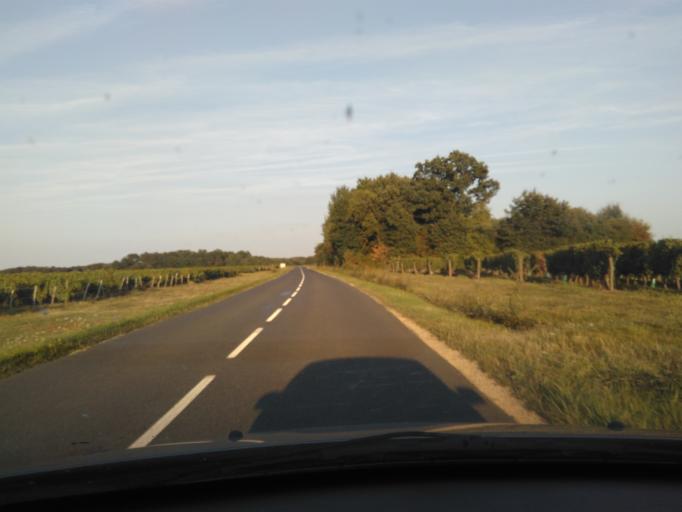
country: FR
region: Pays de la Loire
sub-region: Departement de Maine-et-Loire
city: Saint-Saturnin-sur-Loire
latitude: 47.3880
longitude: -0.4165
